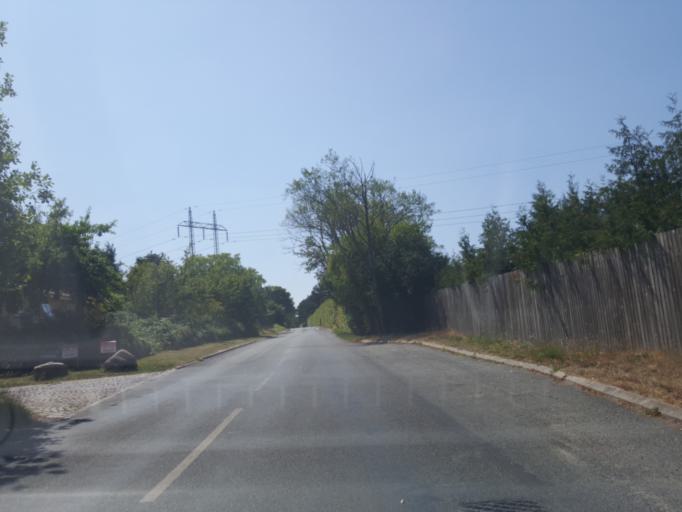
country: DK
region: Capital Region
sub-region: Fredensborg Kommune
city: Kokkedal
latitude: 55.9280
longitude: 12.4652
